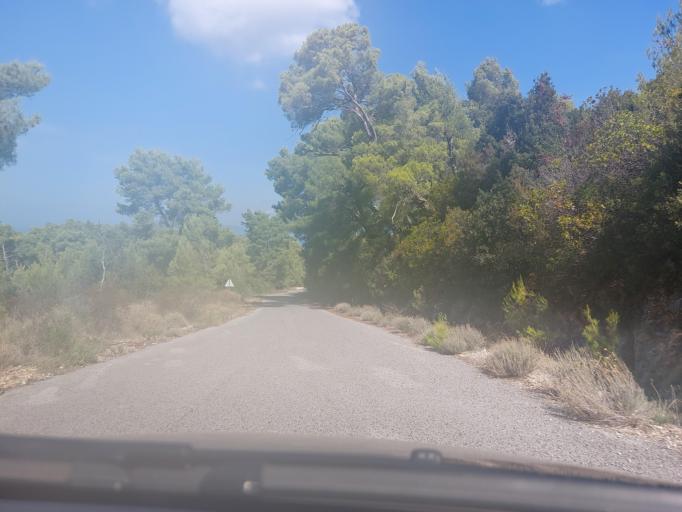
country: HR
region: Dubrovacko-Neretvanska
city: Smokvica
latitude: 42.7446
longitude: 16.8464
